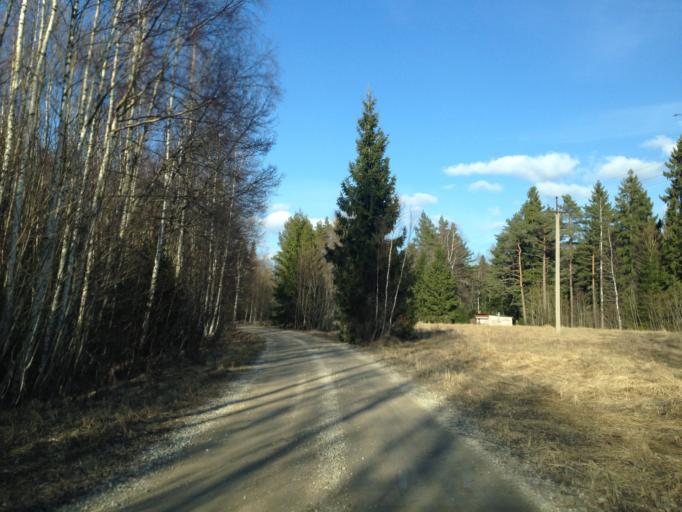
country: EE
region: Harju
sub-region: Nissi vald
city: Turba
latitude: 59.1336
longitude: 24.1685
